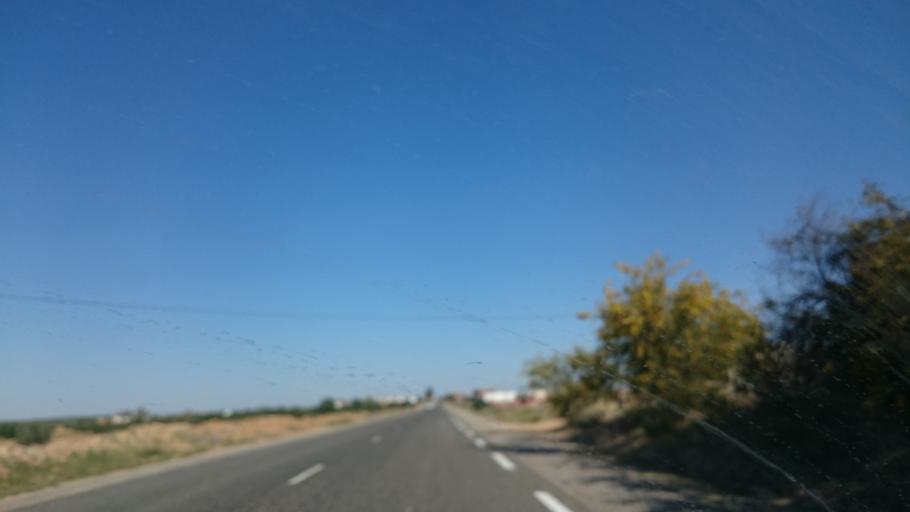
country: TN
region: Safaqis
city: Sfax
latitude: 34.7650
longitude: 10.5123
